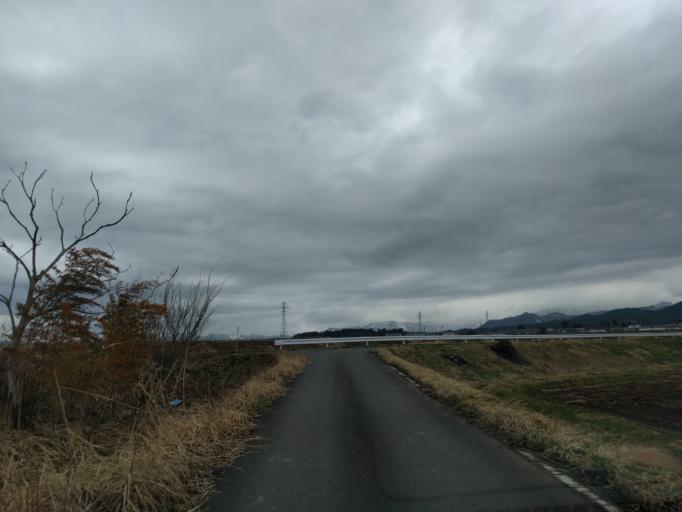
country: JP
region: Fukushima
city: Kitakata
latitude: 37.6510
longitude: 139.9144
